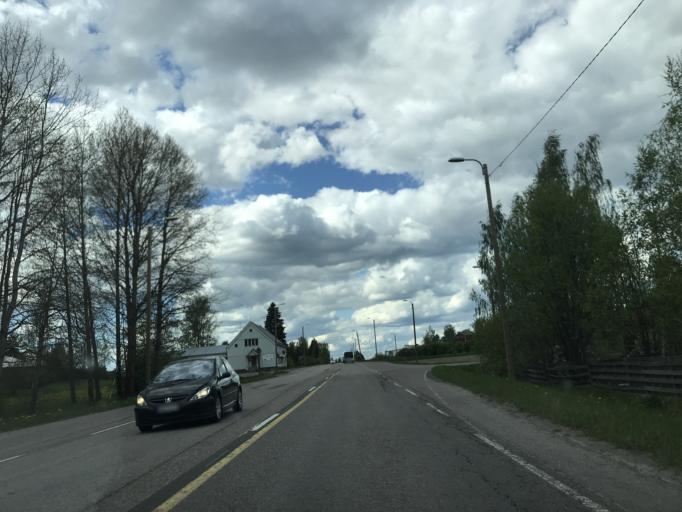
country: FI
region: Uusimaa
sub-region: Helsinki
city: Nurmijaervi
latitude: 60.4395
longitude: 24.7044
